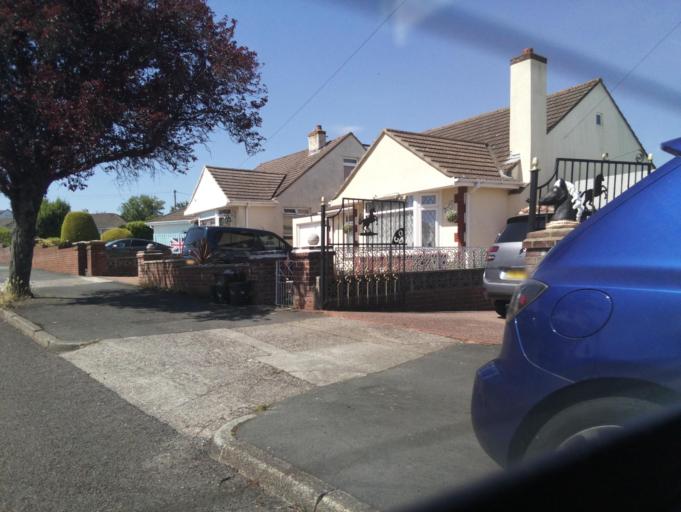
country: GB
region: England
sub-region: Borough of Torbay
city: Paignton
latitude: 50.4536
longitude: -3.5680
